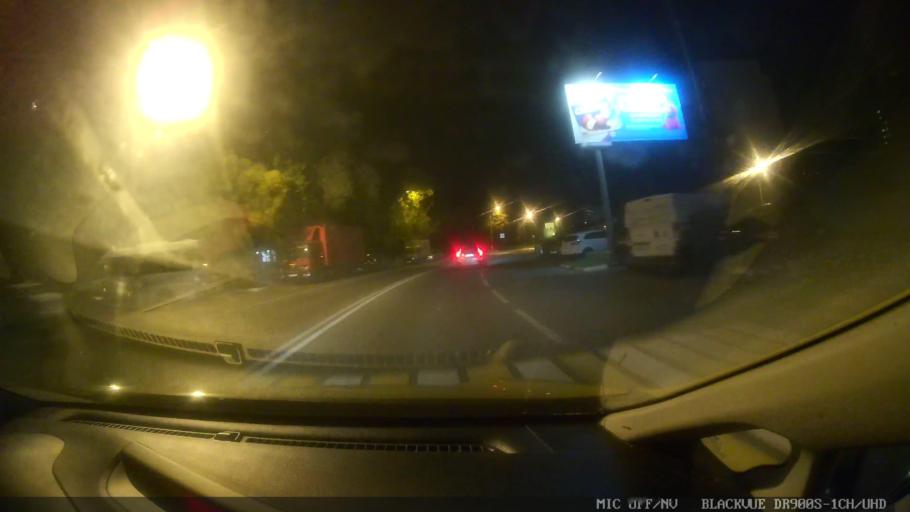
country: RU
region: Moskovskaya
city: Reutov
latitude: 55.7478
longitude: 37.8547
